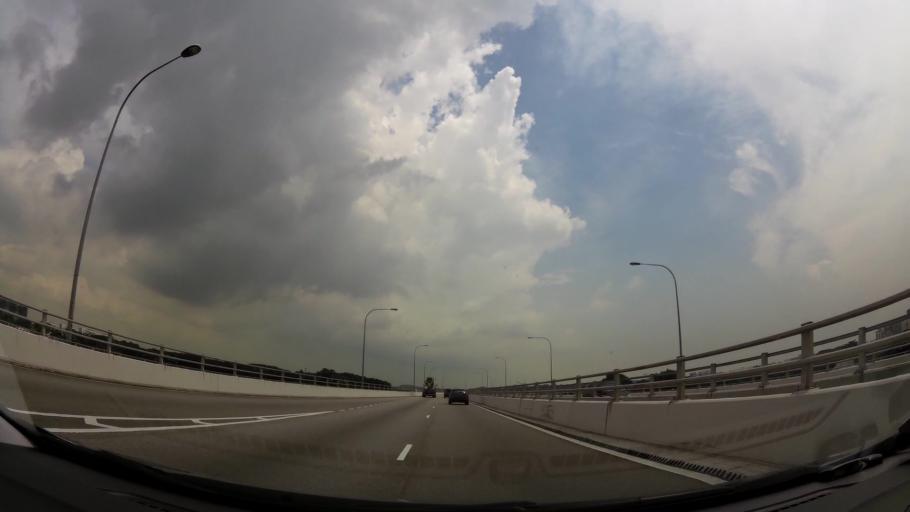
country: SG
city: Singapore
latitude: 1.3428
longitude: 103.8899
